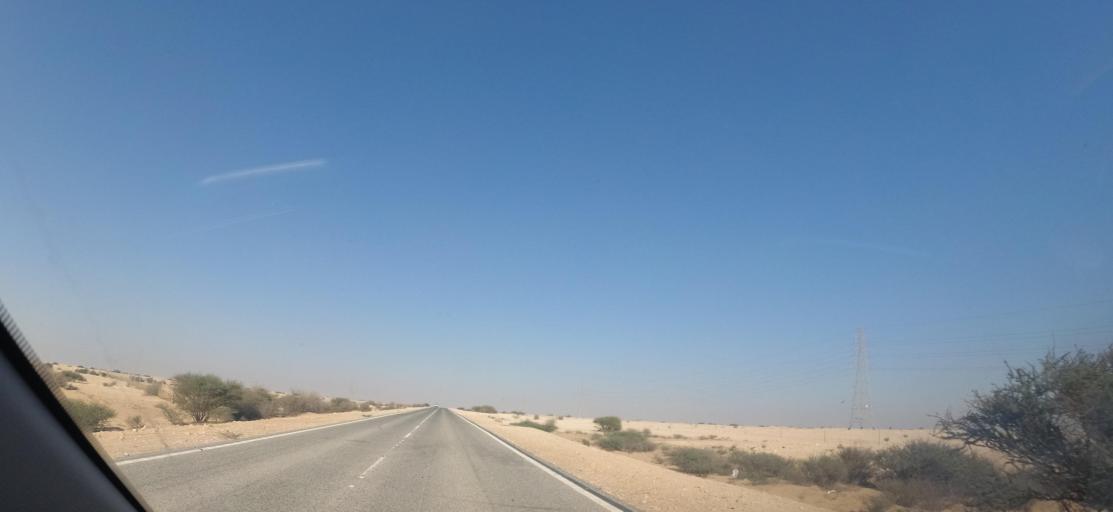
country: QA
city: Al Jumayliyah
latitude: 25.6343
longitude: 51.0984
